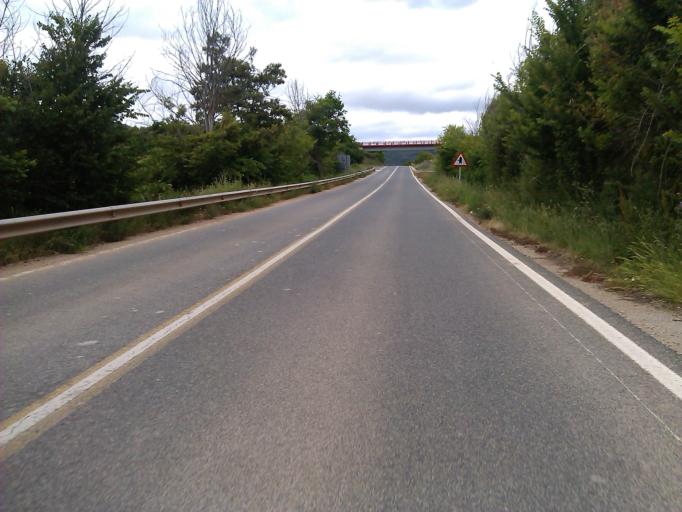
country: ES
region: Navarre
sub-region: Provincia de Navarra
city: Cirauqui
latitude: 42.6780
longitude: -1.8940
